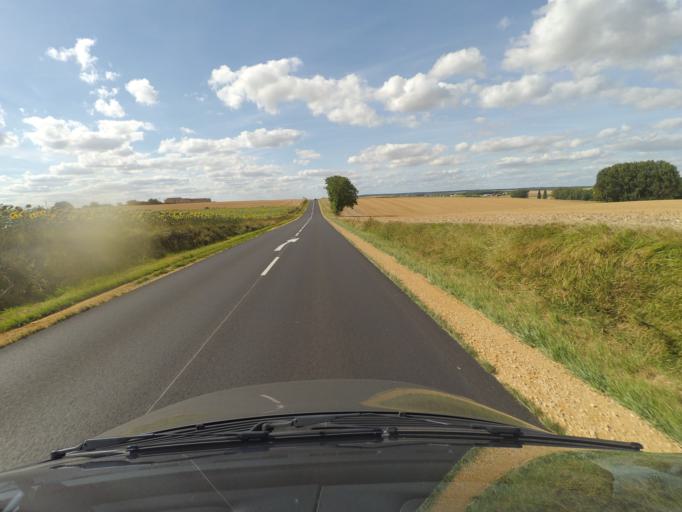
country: FR
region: Poitou-Charentes
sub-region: Departement de la Vienne
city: Saint-Gervais-les-Trois-Clochers
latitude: 46.9203
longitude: 0.4390
